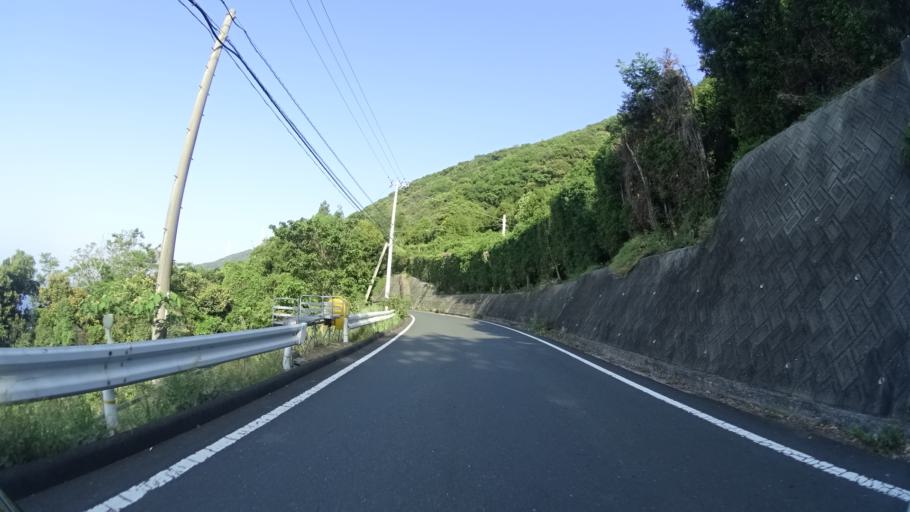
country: JP
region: Ehime
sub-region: Nishiuwa-gun
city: Ikata-cho
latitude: 33.3894
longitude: 132.1015
